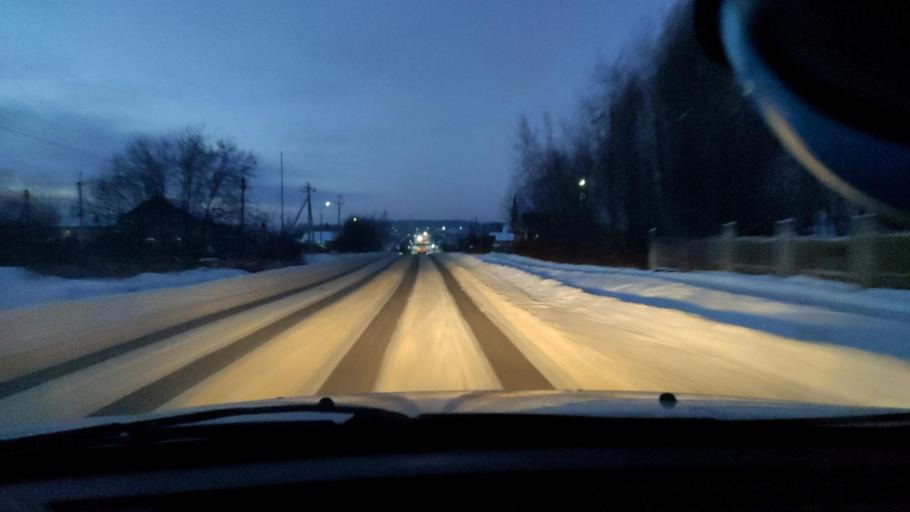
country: RU
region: Perm
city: Kultayevo
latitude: 57.8969
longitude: 55.9303
